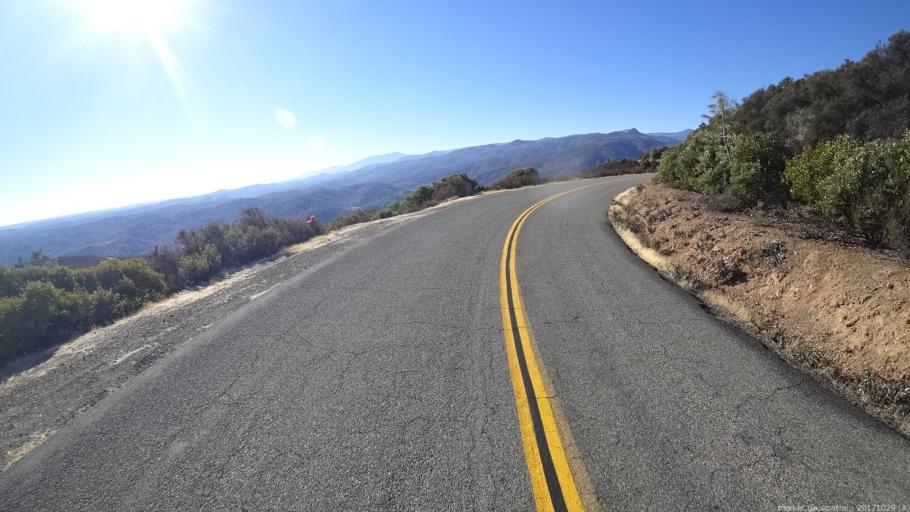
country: US
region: California
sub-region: Trinity County
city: Lewiston
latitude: 40.3668
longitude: -122.8472
